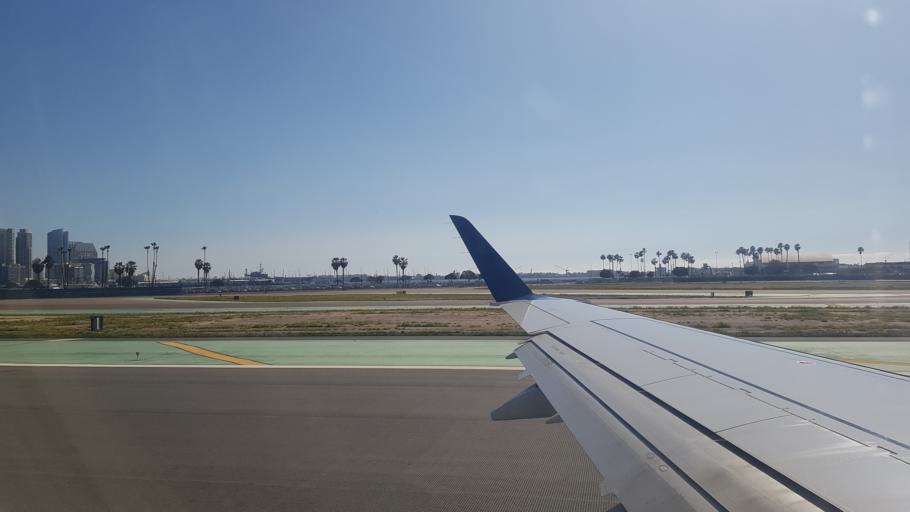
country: US
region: California
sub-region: San Diego County
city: San Diego
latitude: 32.7309
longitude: -117.1786
